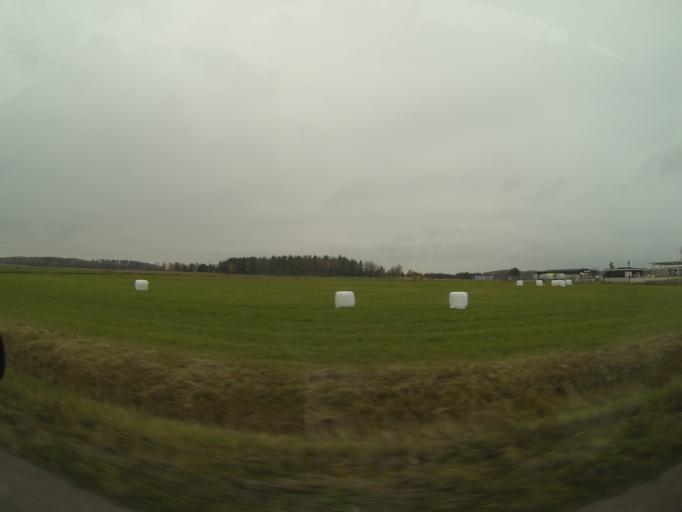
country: SE
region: Vaestmanland
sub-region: Kopings Kommun
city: Koping
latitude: 59.5678
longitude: 16.0927
